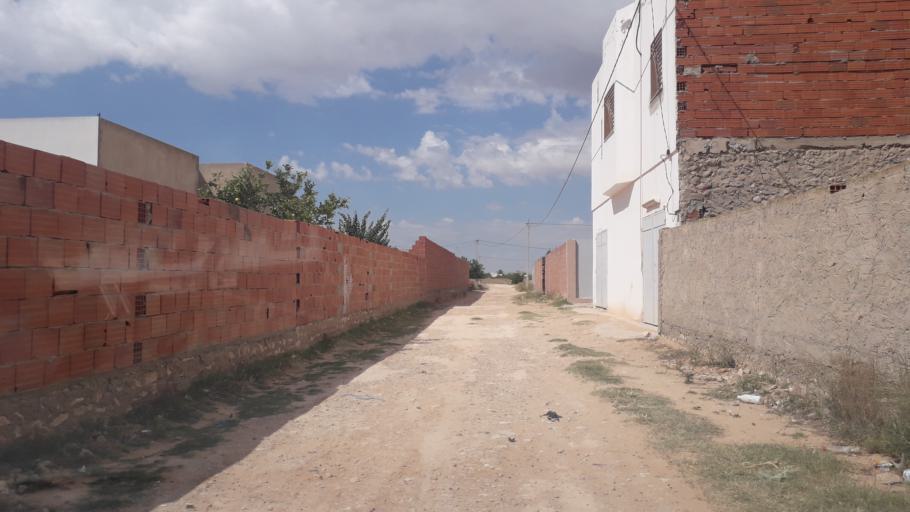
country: TN
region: Safaqis
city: Al Qarmadah
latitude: 34.8385
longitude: 10.7739
